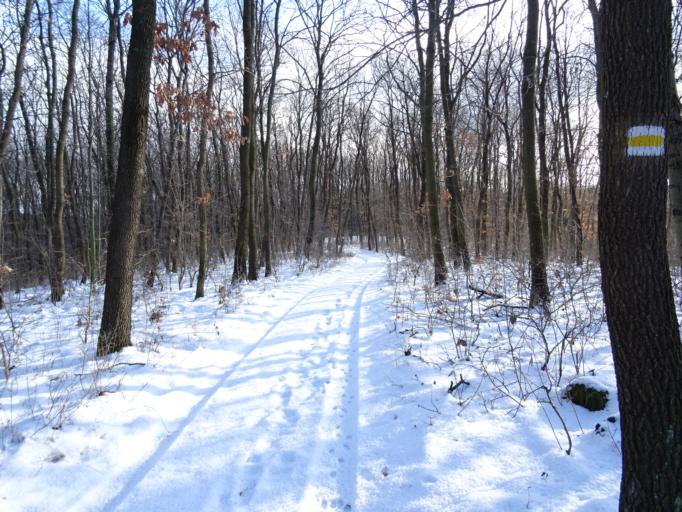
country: HU
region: Komarom-Esztergom
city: Oroszlany
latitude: 47.4769
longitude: 18.3732
